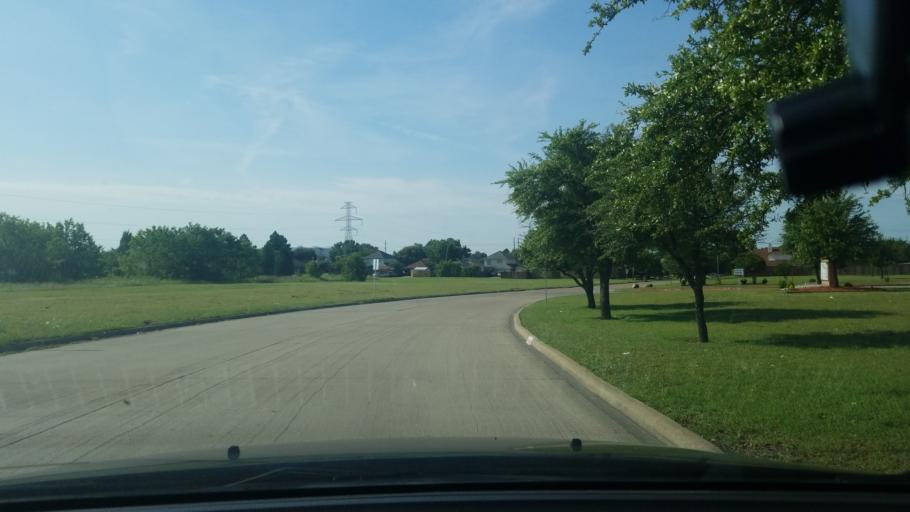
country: US
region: Texas
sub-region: Dallas County
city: Sunnyvale
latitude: 32.7815
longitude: -96.5745
